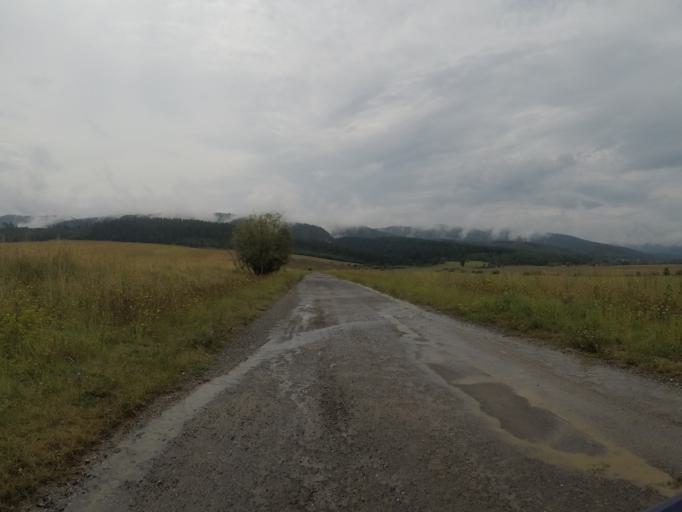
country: SK
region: Kosicky
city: Spisska Nova Ves
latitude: 48.9660
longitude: 20.4517
